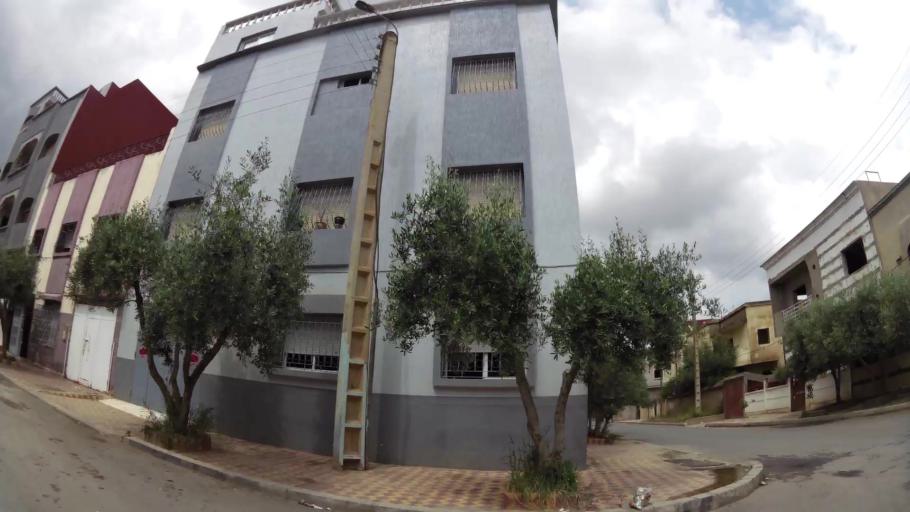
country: MA
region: Rabat-Sale-Zemmour-Zaer
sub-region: Khemisset
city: Tiflet
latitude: 33.8931
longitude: -6.3275
